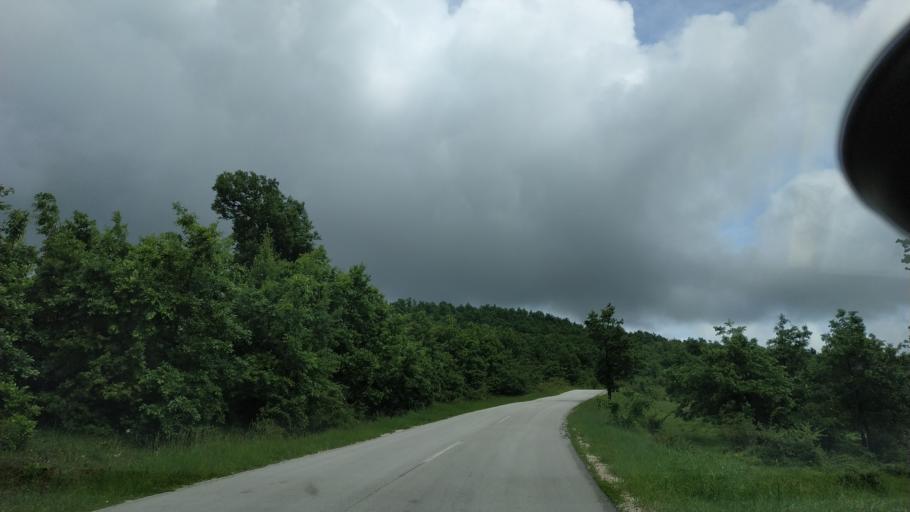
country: RS
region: Central Serbia
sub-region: Zajecarski Okrug
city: Soko Banja
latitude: 43.7155
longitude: 21.9407
